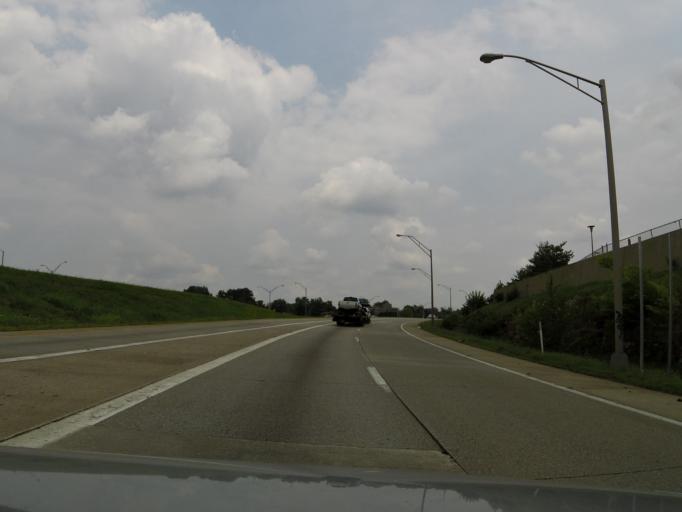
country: US
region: Kentucky
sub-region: Jefferson County
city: Audubon Park
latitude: 38.1897
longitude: -85.7255
